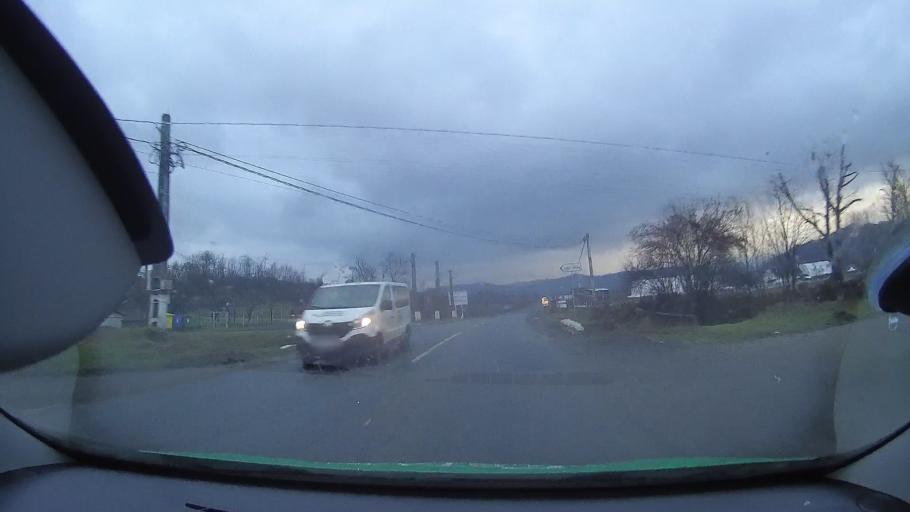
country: RO
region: Hunedoara
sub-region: Municipiul Brad
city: Brad
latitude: 46.1548
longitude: 22.7647
